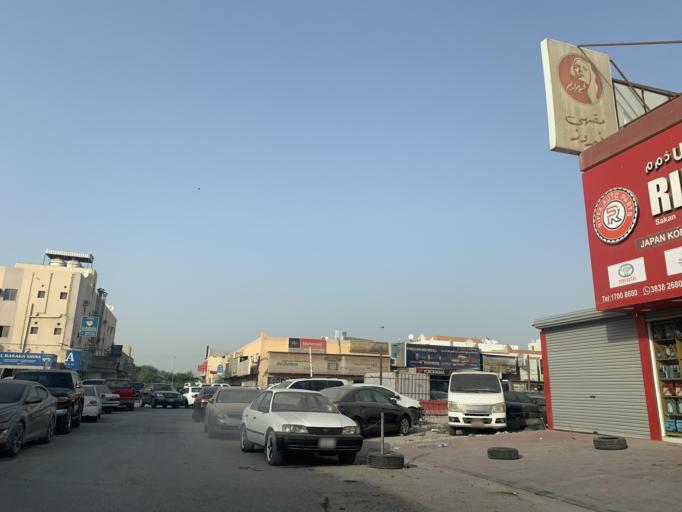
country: BH
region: Central Governorate
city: Madinat Hamad
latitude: 26.1465
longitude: 50.4878
